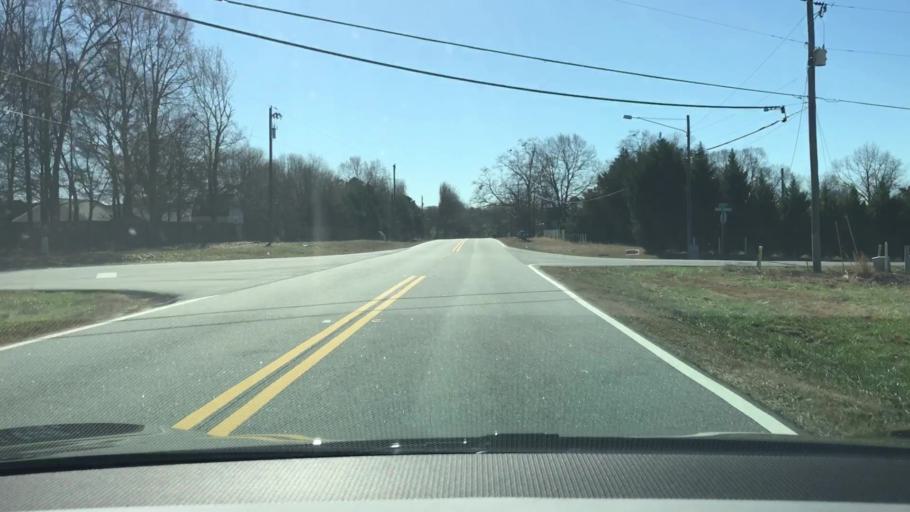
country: US
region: Georgia
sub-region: Walton County
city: Monroe
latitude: 33.8463
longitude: -83.7359
